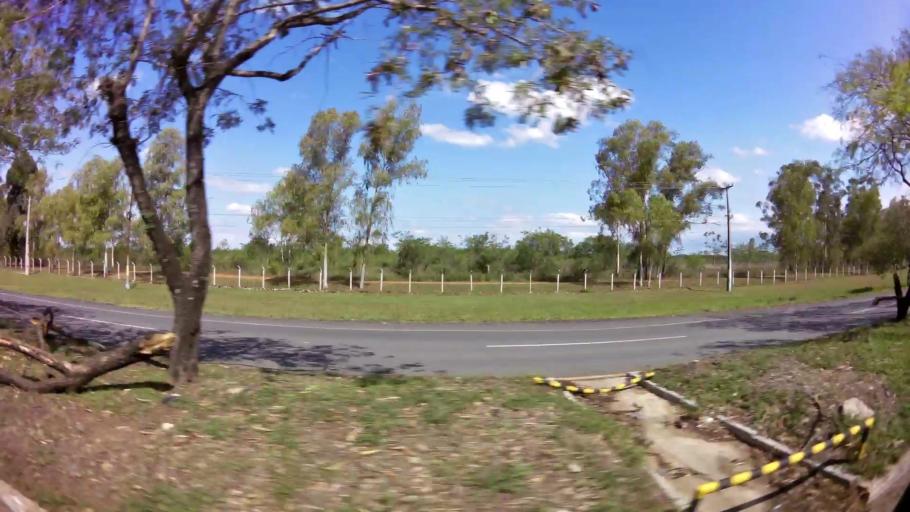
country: PY
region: Central
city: Fernando de la Mora
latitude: -25.2628
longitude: -57.5332
